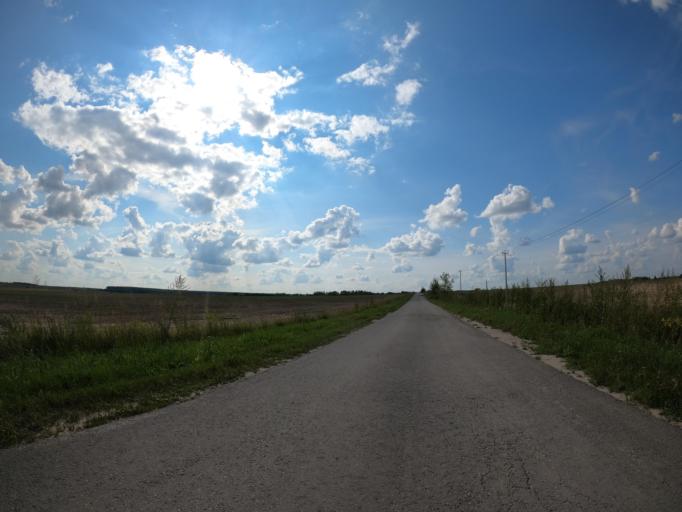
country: RU
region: Moskovskaya
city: Troitskoye
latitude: 55.2378
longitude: 38.5039
